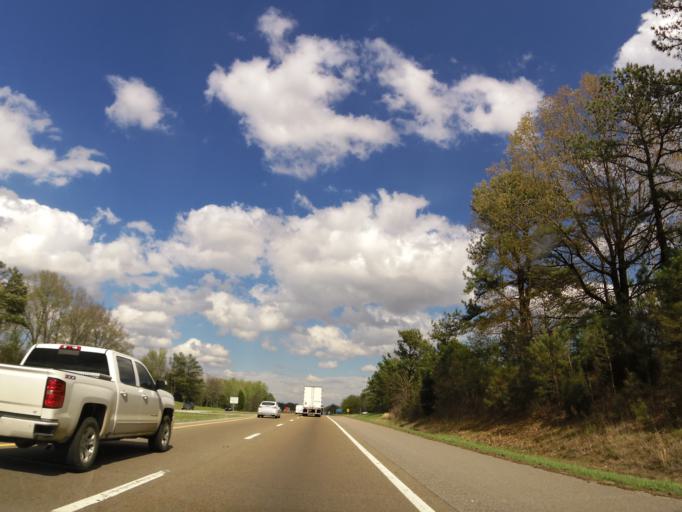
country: US
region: Tennessee
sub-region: Crockett County
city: Bells
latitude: 35.6226
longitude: -88.9825
